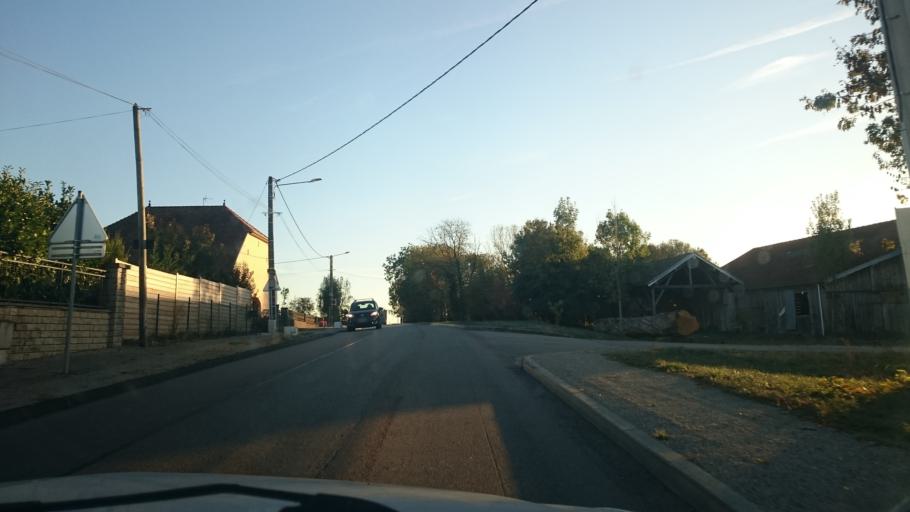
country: FR
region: Franche-Comte
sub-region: Departement du Doubs
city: Quingey
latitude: 47.0521
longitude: 5.8788
